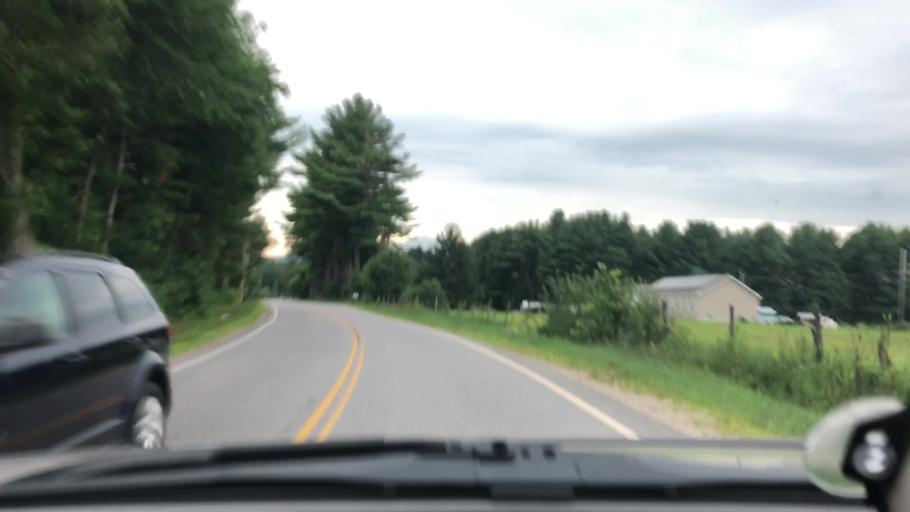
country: US
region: New York
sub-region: Saratoga County
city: Corinth
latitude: 43.2232
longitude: -73.8156
